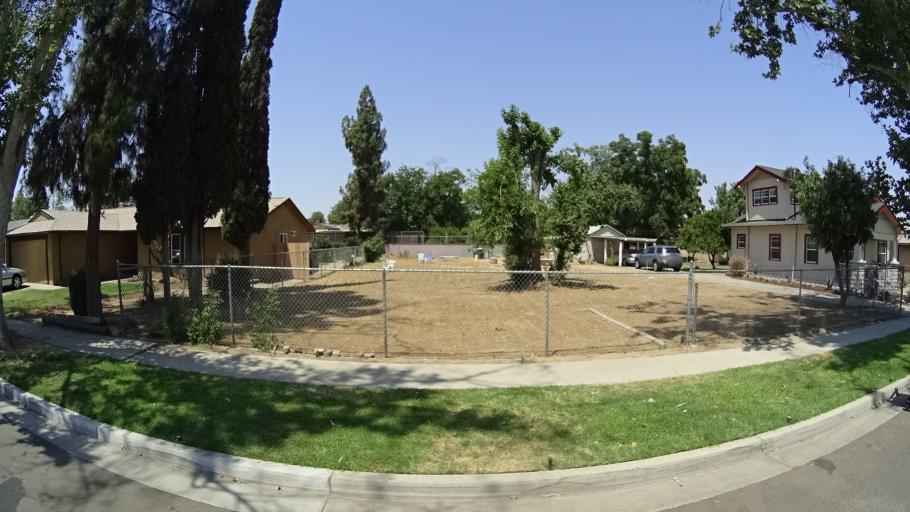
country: US
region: California
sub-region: Fresno County
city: Fresno
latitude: 36.7205
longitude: -119.7931
